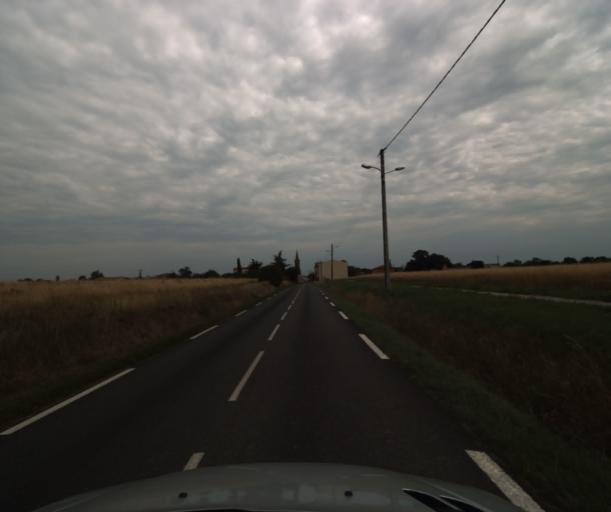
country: FR
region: Midi-Pyrenees
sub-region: Departement de la Haute-Garonne
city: Lacasse
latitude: 43.4196
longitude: 1.2774
